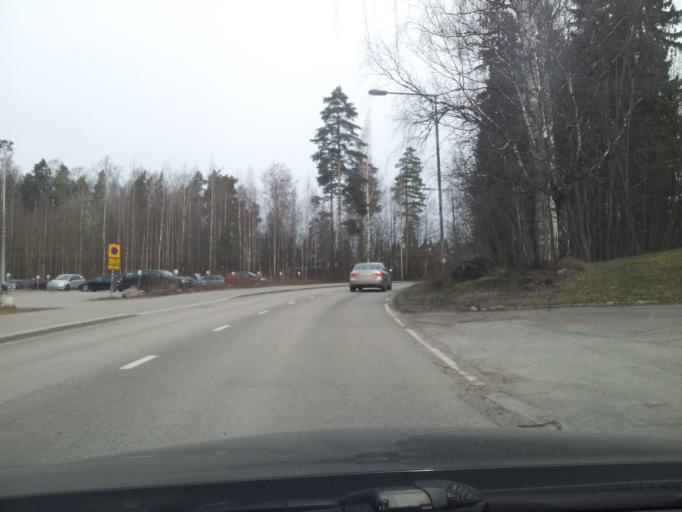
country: FI
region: Uusimaa
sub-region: Helsinki
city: Otaniemi
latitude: 60.1888
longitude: 24.7972
